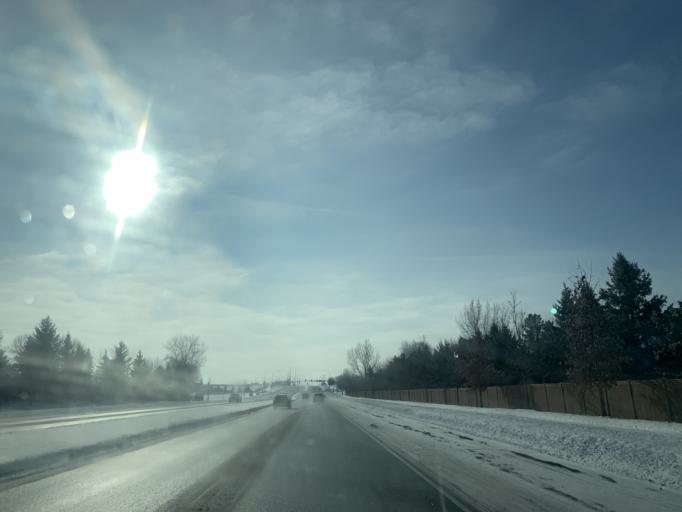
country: US
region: Minnesota
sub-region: Dakota County
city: Apple Valley
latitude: 44.7015
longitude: -93.2177
